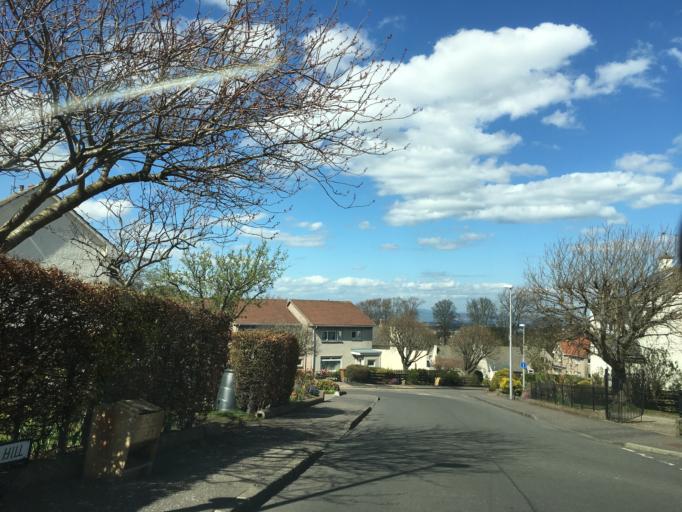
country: GB
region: Scotland
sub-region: Edinburgh
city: Colinton
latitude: 55.9040
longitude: -3.2132
